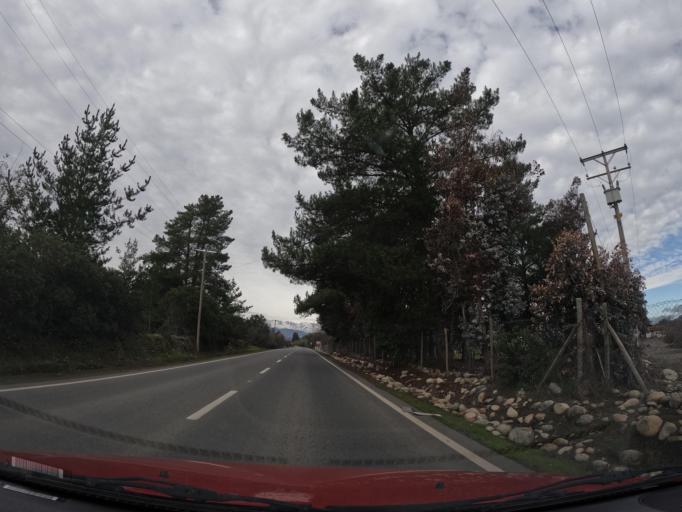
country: CL
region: Maule
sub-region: Provincia de Linares
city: Linares
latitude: -35.9060
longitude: -71.5017
